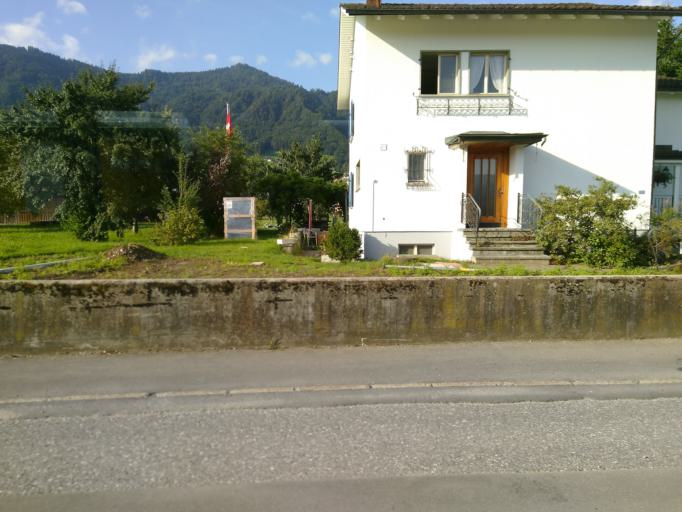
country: CH
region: Schwyz
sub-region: Bezirk March
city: Reichenburg
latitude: 47.1722
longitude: 8.9840
